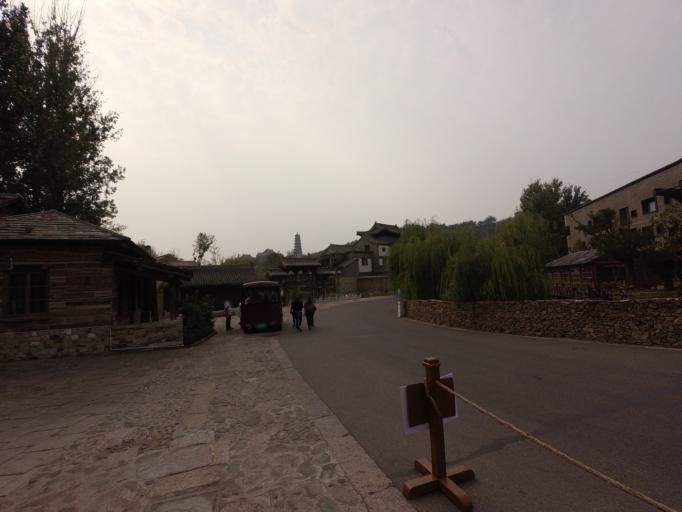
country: CN
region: Beijing
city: Xinchengzi
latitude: 40.6512
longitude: 117.2683
